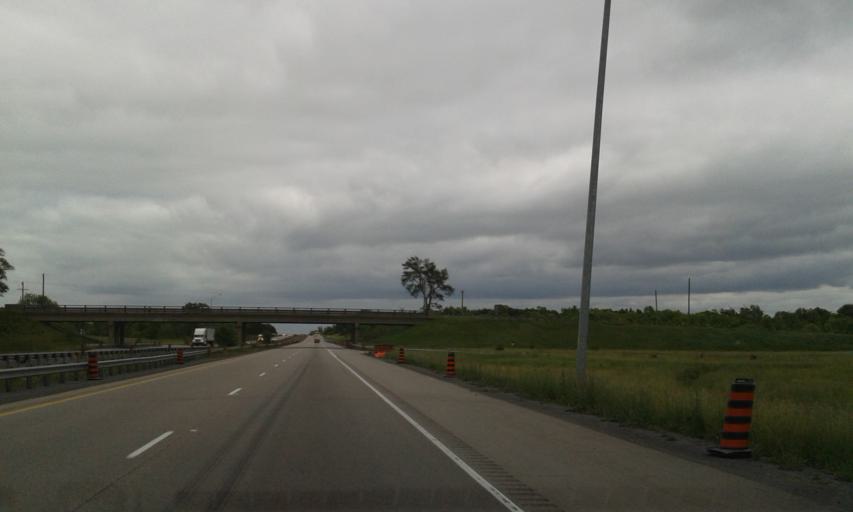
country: CA
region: Ontario
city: Skatepark
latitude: 44.2823
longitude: -76.7184
